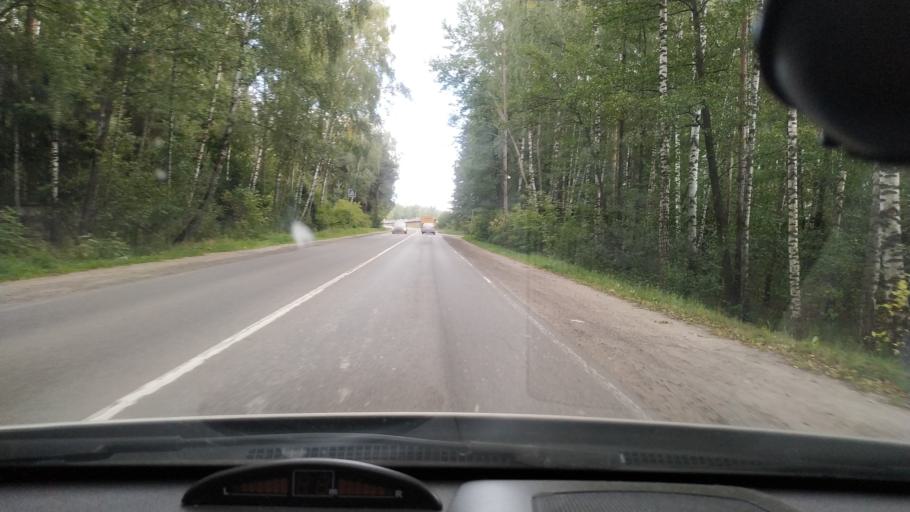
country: RU
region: Moskovskaya
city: Chornaya
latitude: 55.7664
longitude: 38.0646
